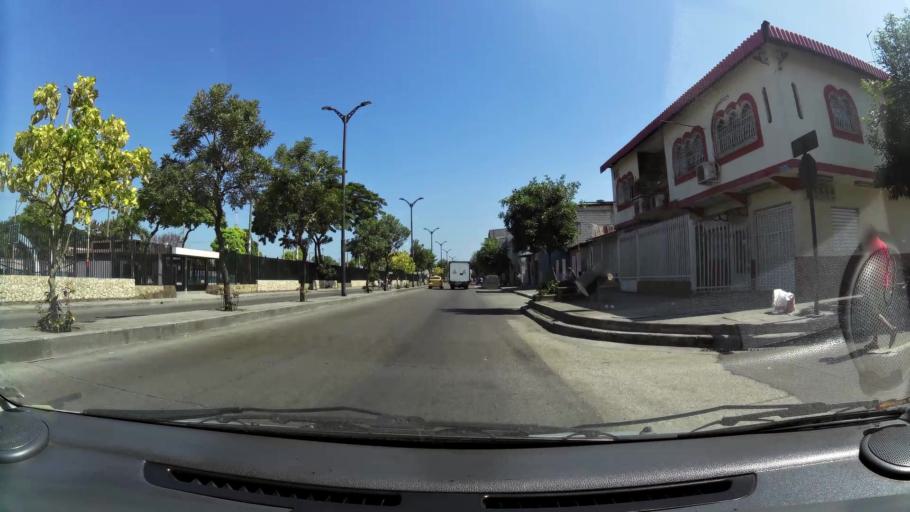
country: EC
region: Guayas
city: Guayaquil
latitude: -2.2127
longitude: -79.9326
